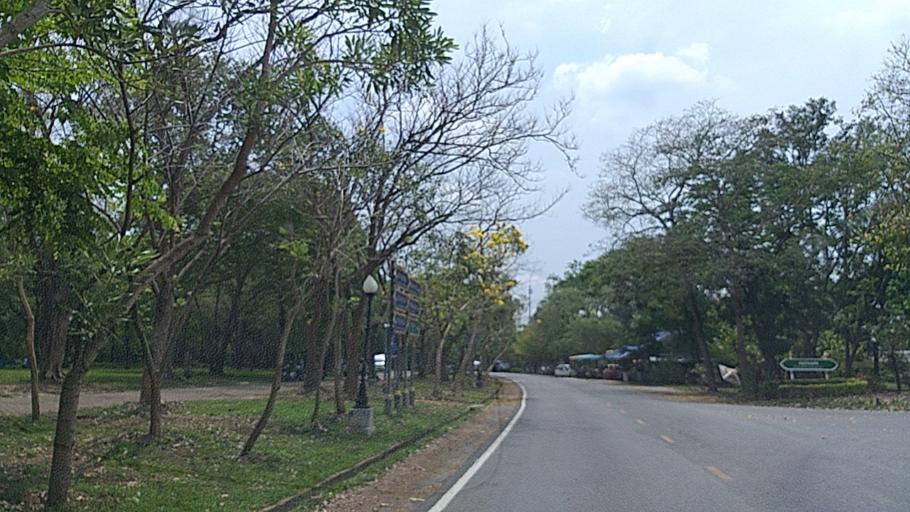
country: TH
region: Bangkok
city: Thawi Watthana
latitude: 13.7751
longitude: 100.3175
